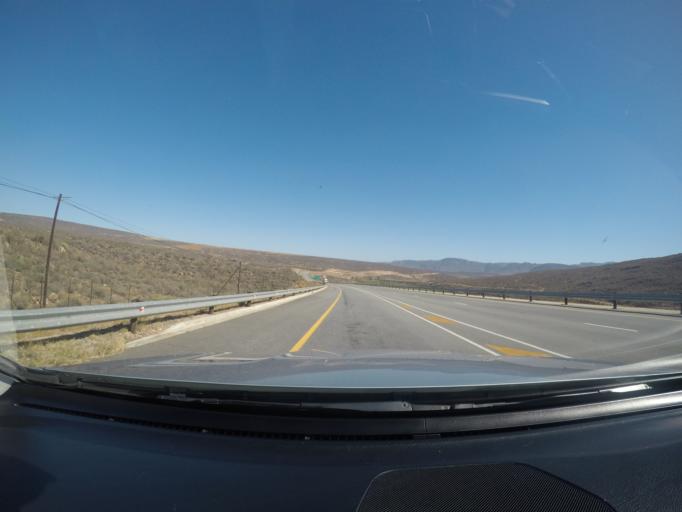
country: ZA
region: Western Cape
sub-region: West Coast District Municipality
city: Clanwilliam
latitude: -32.1831
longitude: 18.8715
